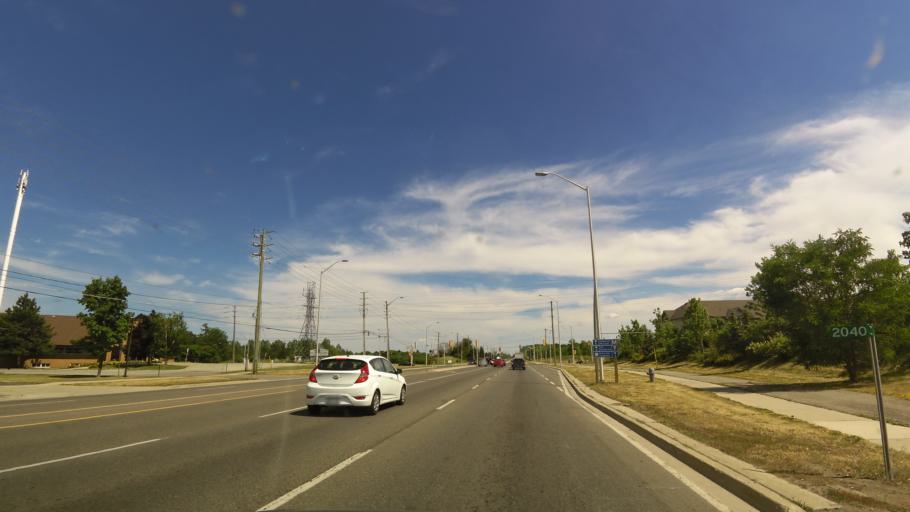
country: CA
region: Ontario
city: Oakville
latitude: 43.4238
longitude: -79.7602
